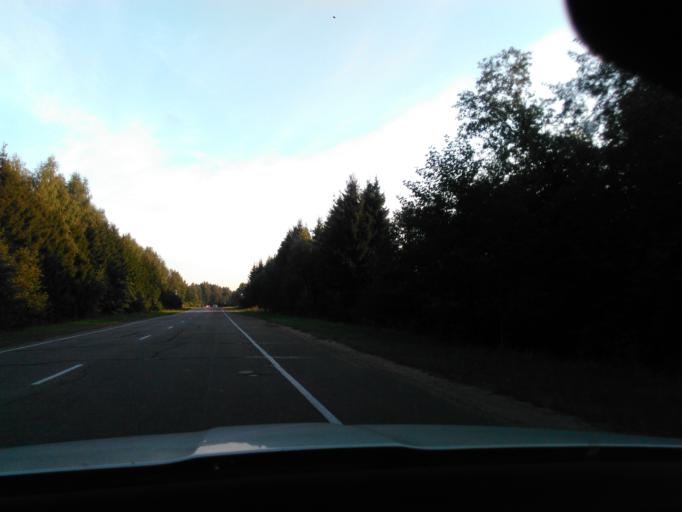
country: RU
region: Tverskaya
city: Konakovo
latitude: 56.6604
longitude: 36.7163
